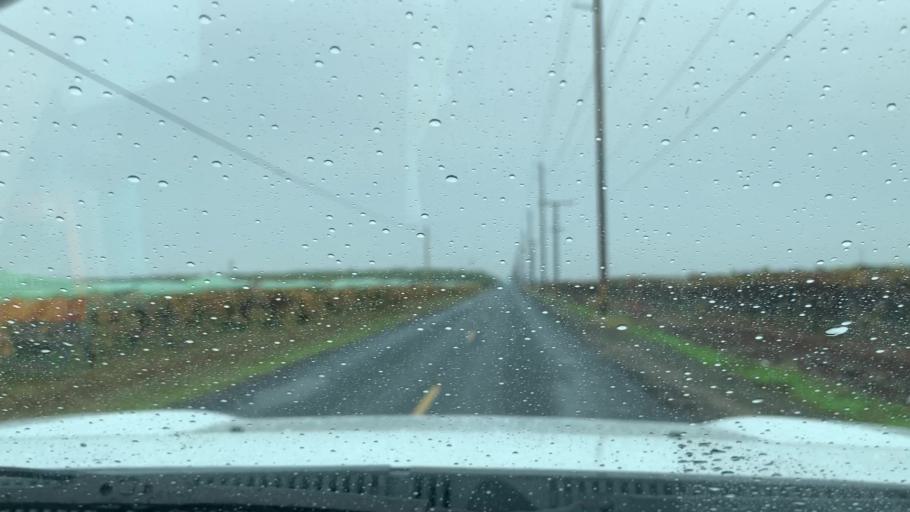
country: US
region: California
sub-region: Tulare County
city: Earlimart
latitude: 35.8339
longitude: -119.2445
